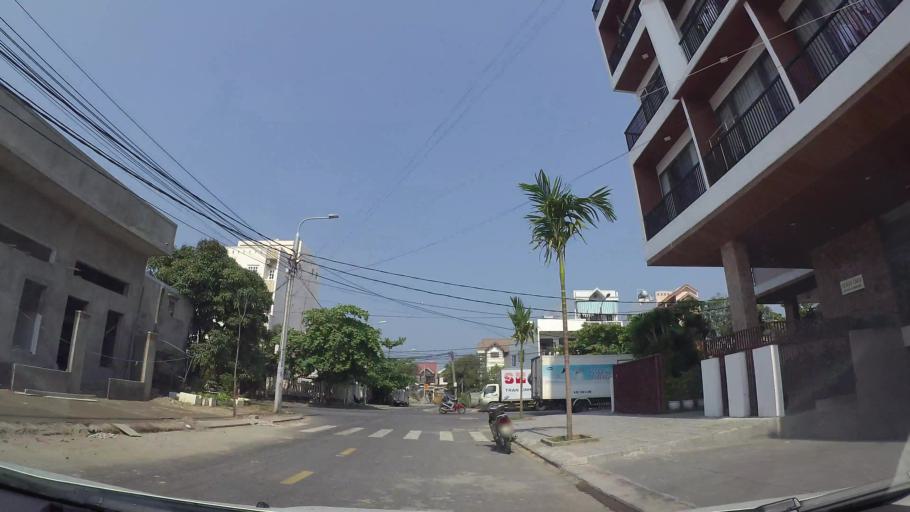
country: VN
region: Da Nang
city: Ngu Hanh Son
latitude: 16.0385
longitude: 108.2472
